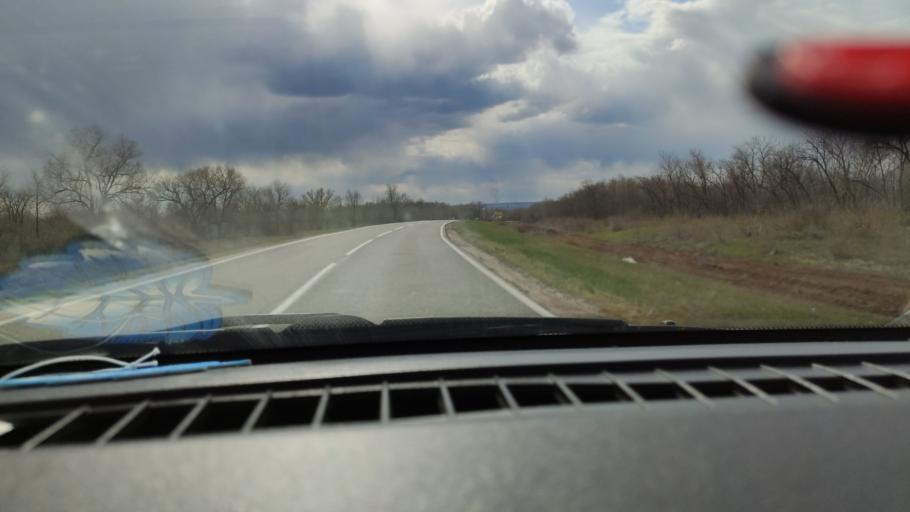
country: RU
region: Saratov
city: Privolzhskiy
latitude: 51.2788
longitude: 45.9522
